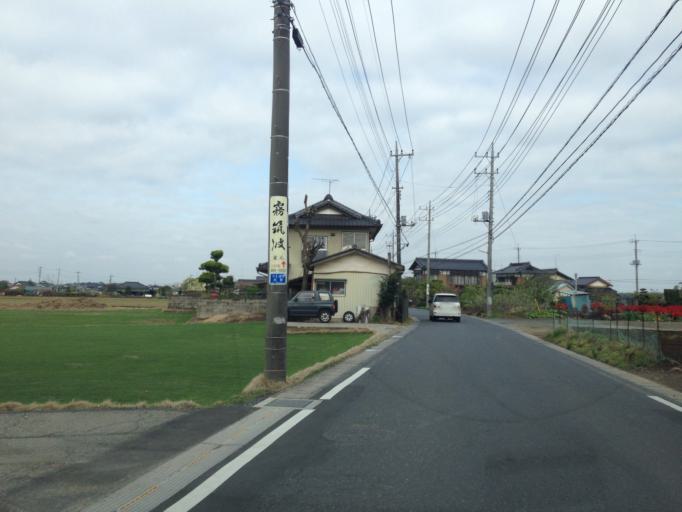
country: JP
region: Ibaraki
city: Ishige
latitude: 36.1419
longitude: 140.0411
